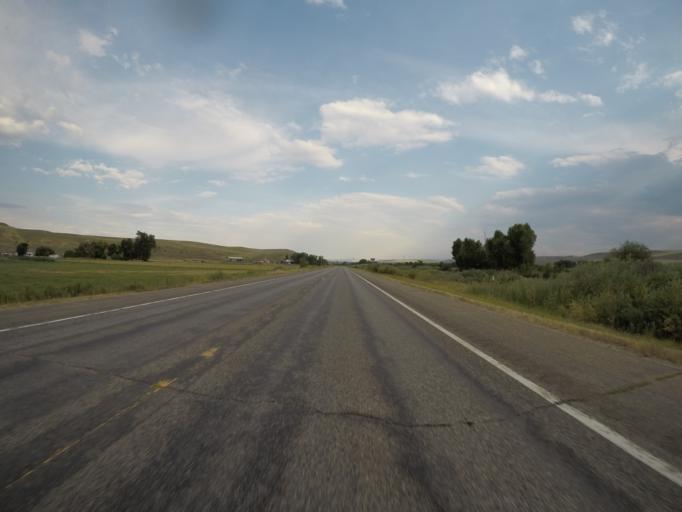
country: US
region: Colorado
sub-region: Routt County
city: Hayden
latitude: 40.5147
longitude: -107.3917
